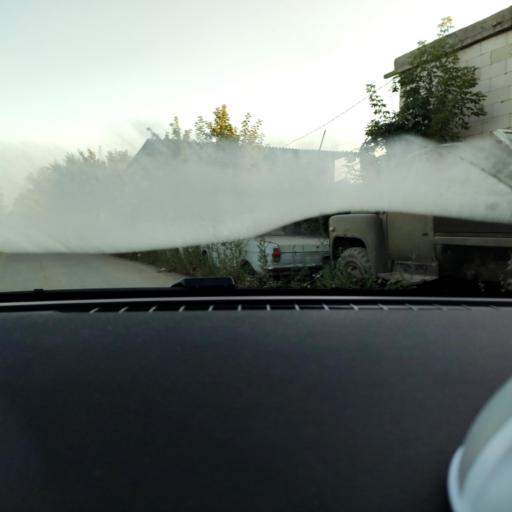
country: RU
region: Samara
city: Petra-Dubrava
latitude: 53.2588
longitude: 50.3059
